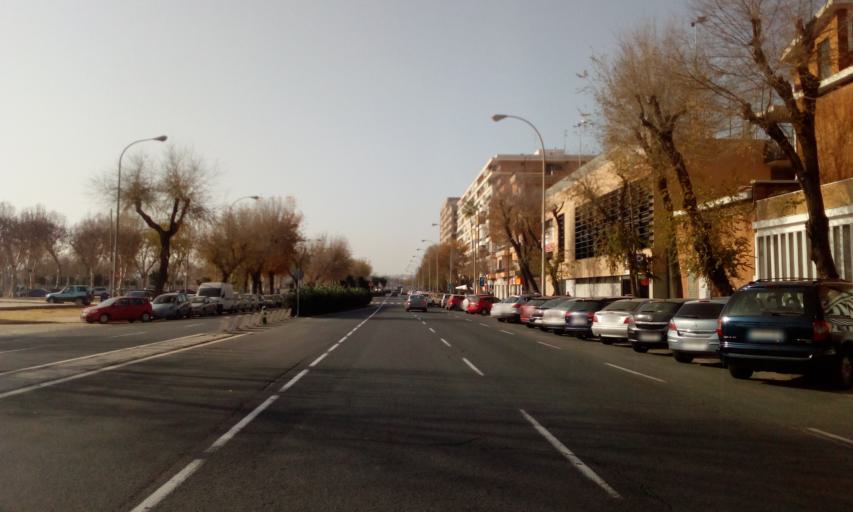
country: ES
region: Andalusia
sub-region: Provincia de Sevilla
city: Sevilla
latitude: 37.3715
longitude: -5.9987
